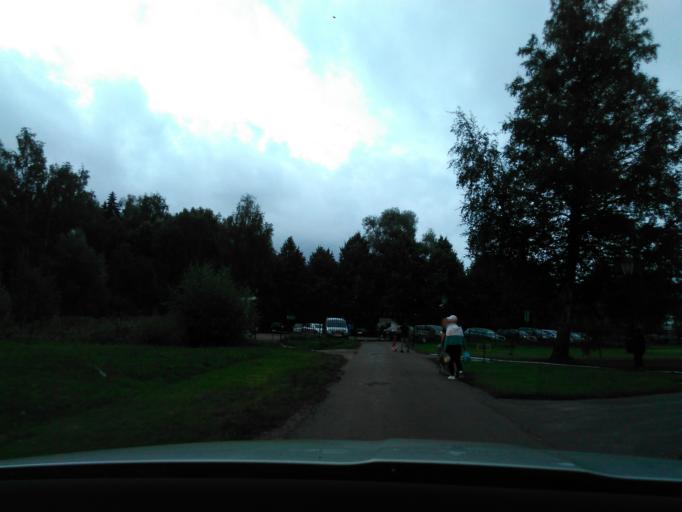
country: RU
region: Tverskaya
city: Konakovo
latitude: 56.6856
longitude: 36.7000
